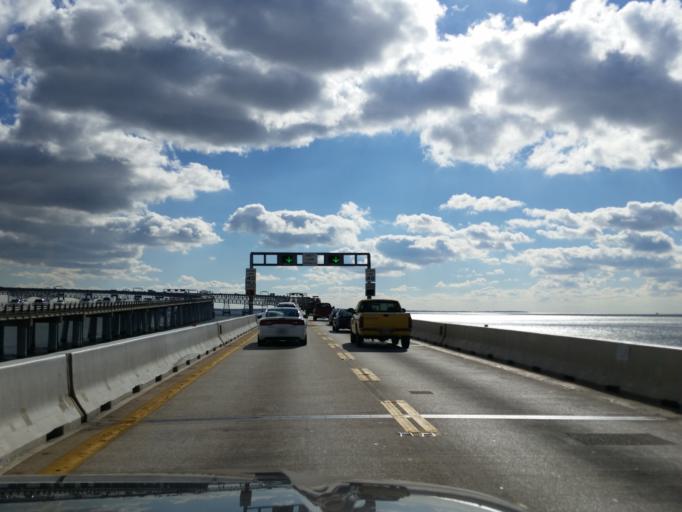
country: US
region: Maryland
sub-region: Anne Arundel County
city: Cape Saint Claire
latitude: 39.0064
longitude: -76.4028
